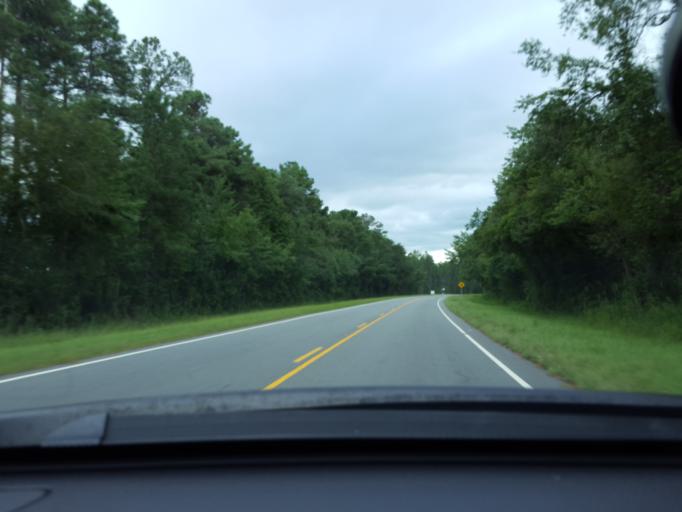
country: US
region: North Carolina
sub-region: Bladen County
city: Elizabethtown
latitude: 34.7162
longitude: -78.4487
